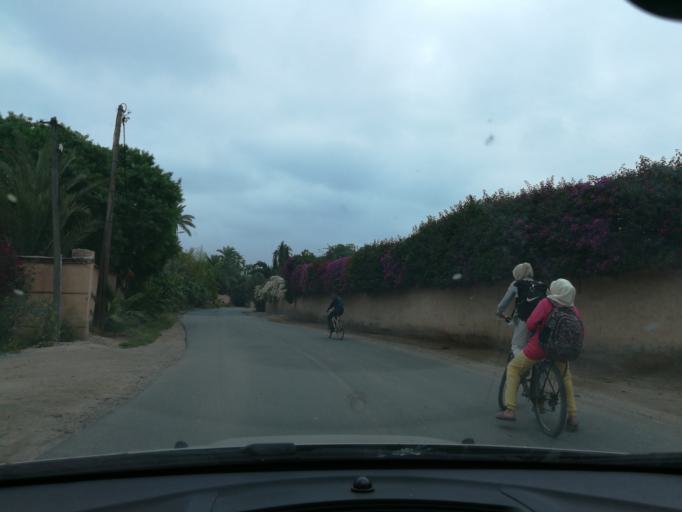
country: MA
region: Marrakech-Tensift-Al Haouz
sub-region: Marrakech
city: Marrakesh
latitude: 31.6737
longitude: -7.9850
